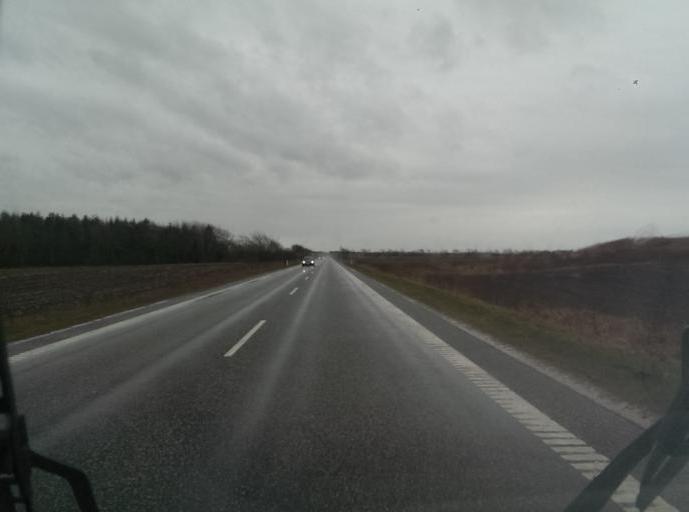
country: DK
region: Central Jutland
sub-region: Ringkobing-Skjern Kommune
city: Tarm
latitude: 55.8334
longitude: 8.4921
